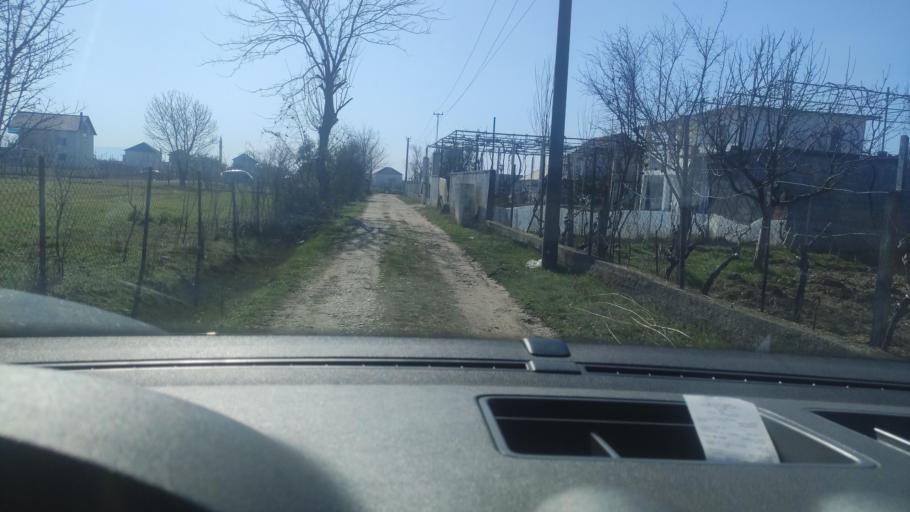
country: AL
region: Shkoder
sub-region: Rrethi i Malesia e Madhe
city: Grude-Fushe
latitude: 42.1651
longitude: 19.4579
